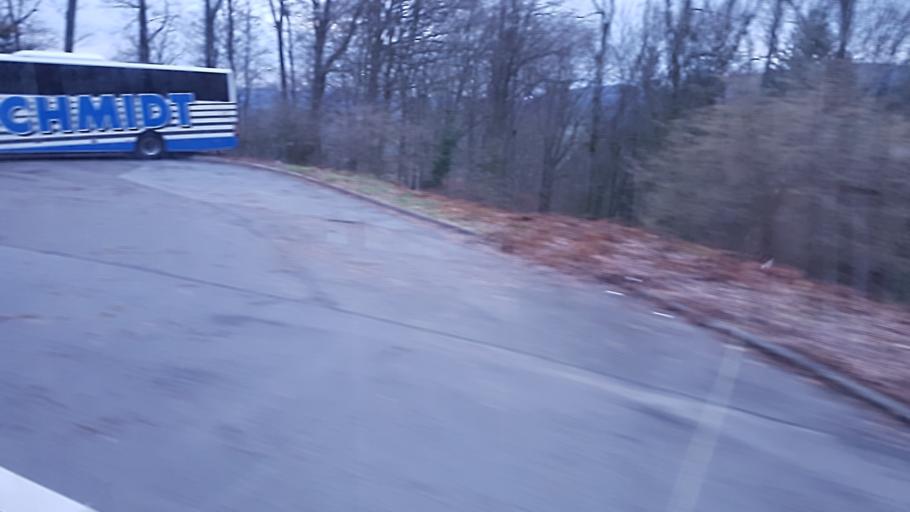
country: DE
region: Hesse
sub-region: Regierungsbezirk Darmstadt
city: Lindenfels
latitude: 49.6900
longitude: 8.7795
